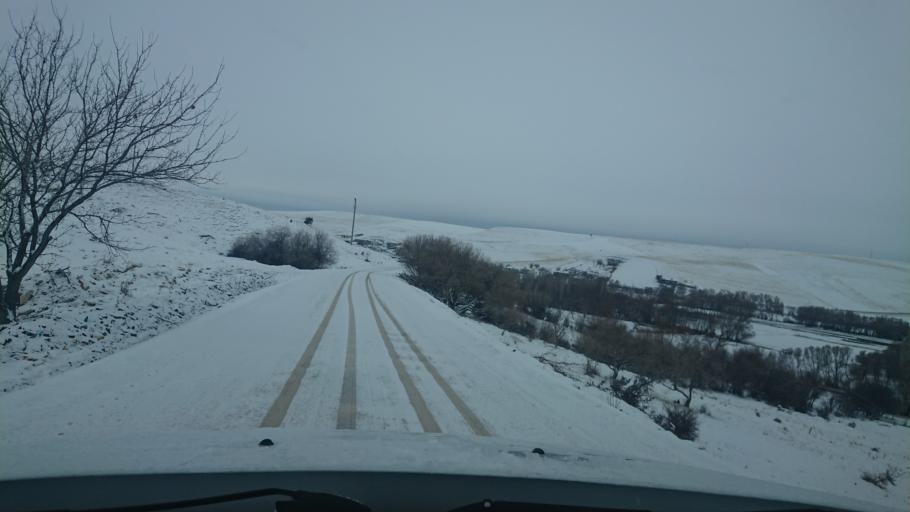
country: TR
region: Aksaray
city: Agacoren
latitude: 38.7558
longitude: 33.8753
